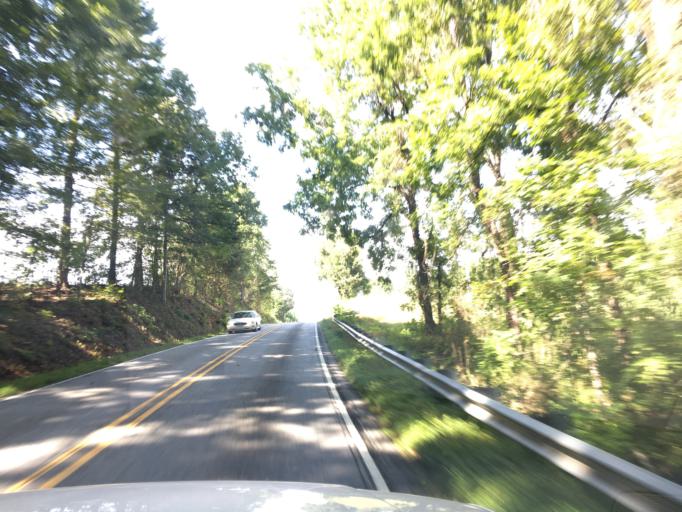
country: US
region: North Carolina
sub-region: Rutherford County
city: Lake Lure
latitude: 35.3514
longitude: -82.1811
